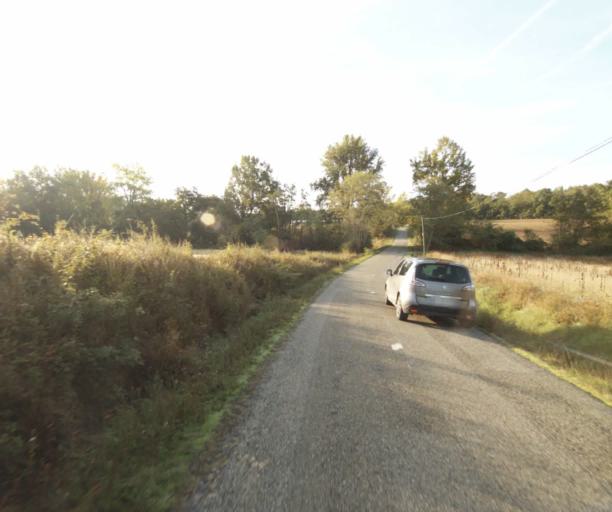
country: FR
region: Midi-Pyrenees
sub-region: Departement du Tarn-et-Garonne
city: Saint-Nauphary
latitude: 43.9444
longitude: 1.4419
